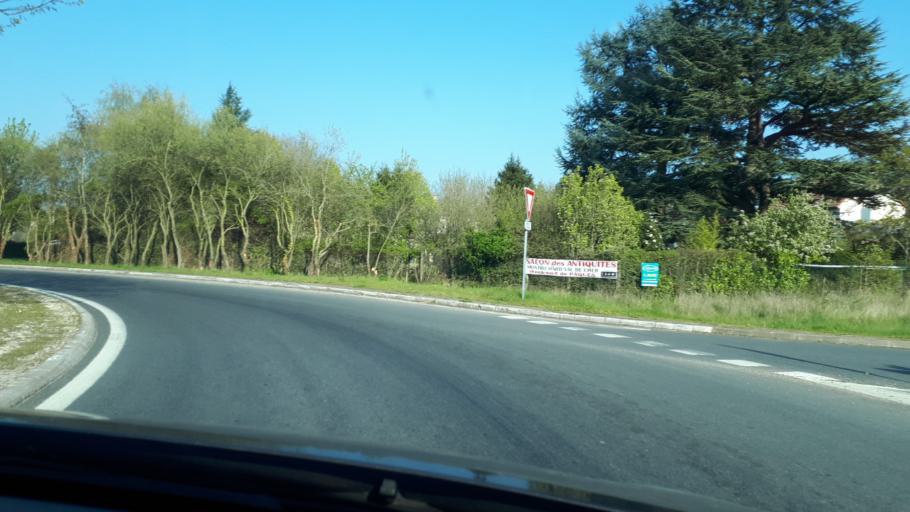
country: FR
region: Centre
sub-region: Departement du Loir-et-Cher
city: Saint-Georges-sur-Cher
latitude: 47.3277
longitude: 1.1328
